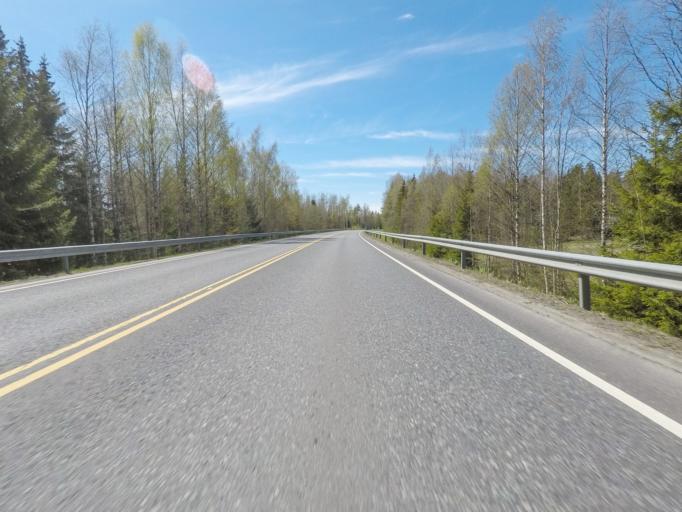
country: FI
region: Haeme
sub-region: Forssa
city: Humppila
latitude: 60.9812
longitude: 23.4390
